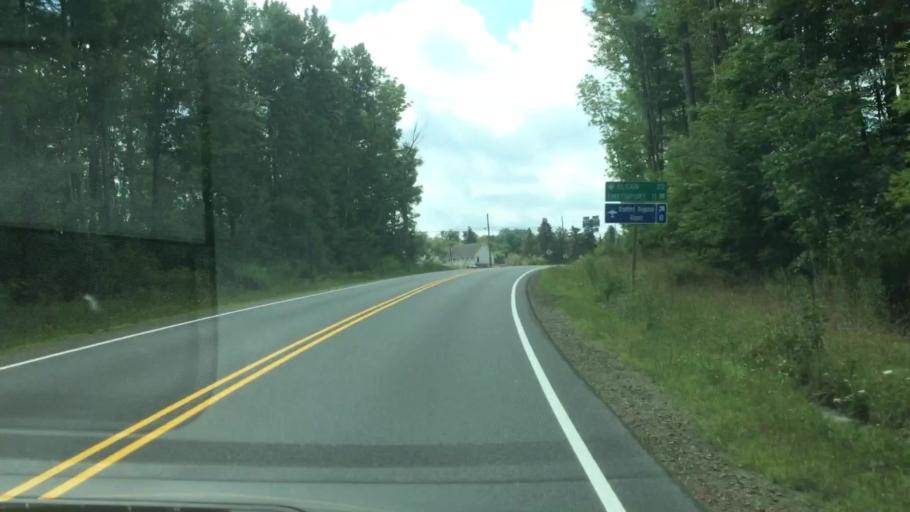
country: US
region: Pennsylvania
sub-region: McKean County
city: Bradford
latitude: 41.8795
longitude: -78.5770
